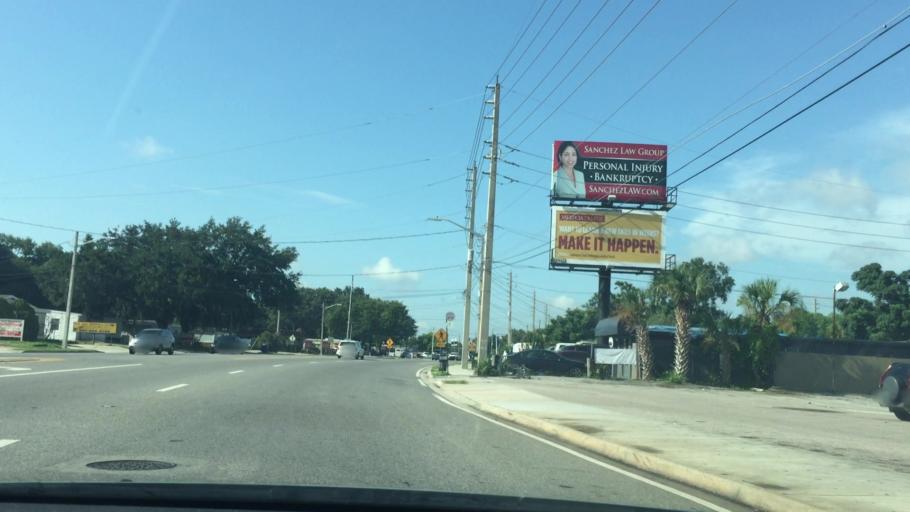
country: US
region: Florida
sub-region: Orange County
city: Pine Hills
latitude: 28.5767
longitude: -81.4516
